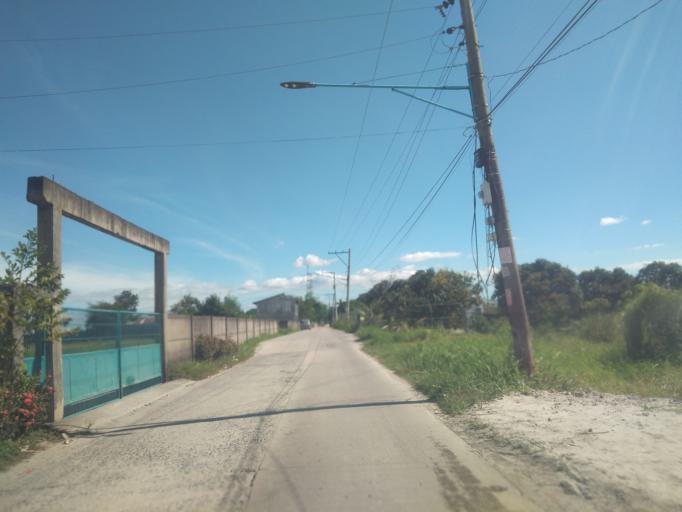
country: PH
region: Central Luzon
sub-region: Province of Pampanga
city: Bacolor
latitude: 15.0083
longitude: 120.6459
